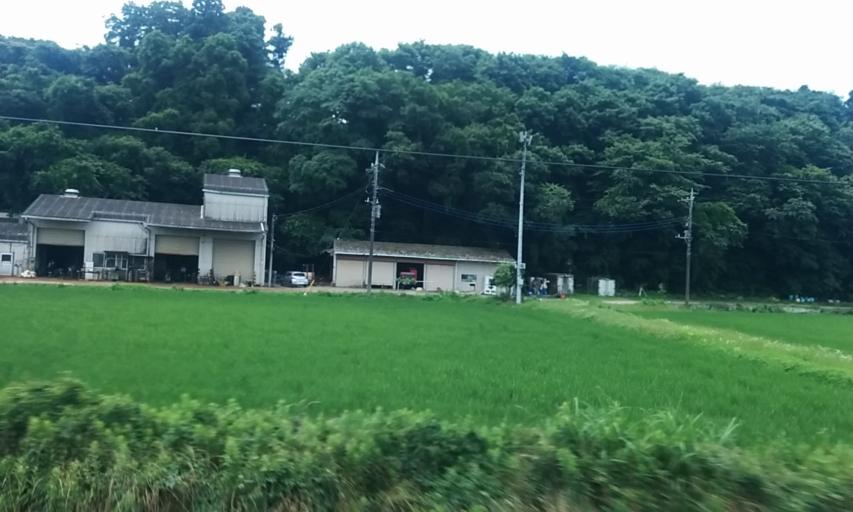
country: JP
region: Chiba
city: Sakura
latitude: 35.7379
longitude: 140.1956
